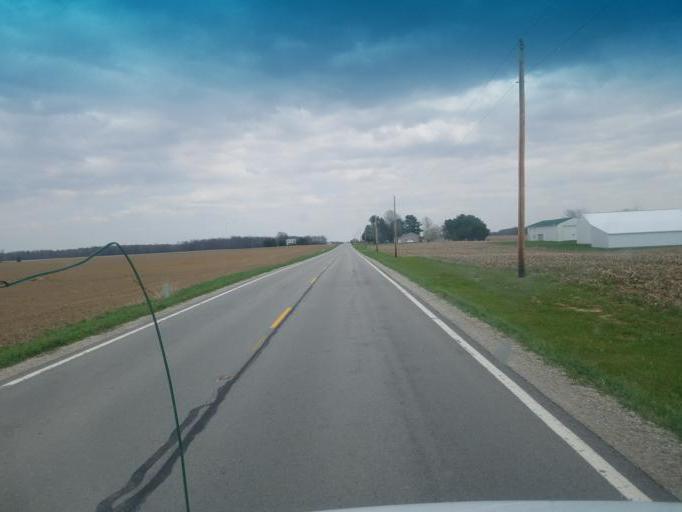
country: US
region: Ohio
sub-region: Seneca County
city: Tiffin
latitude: 40.9500
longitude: -83.1013
